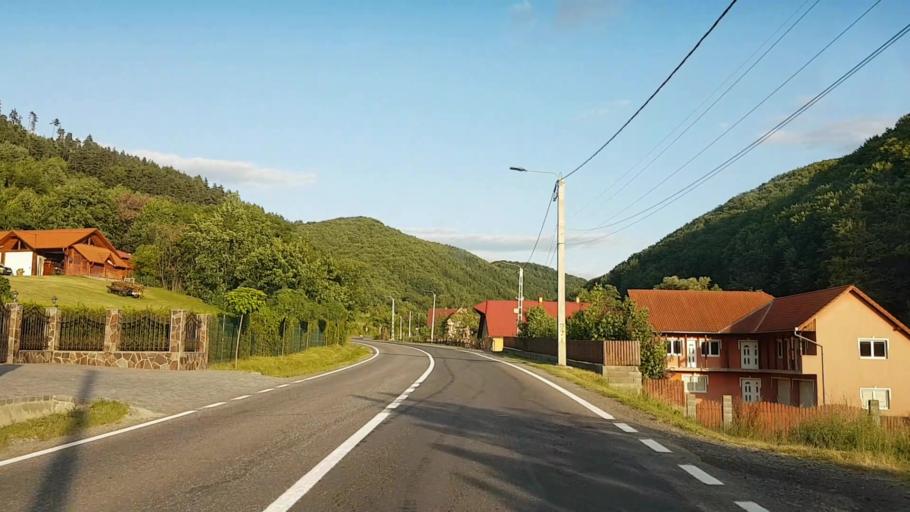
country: RO
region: Harghita
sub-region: Comuna Corund
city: Corund
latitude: 46.4673
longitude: 25.2022
